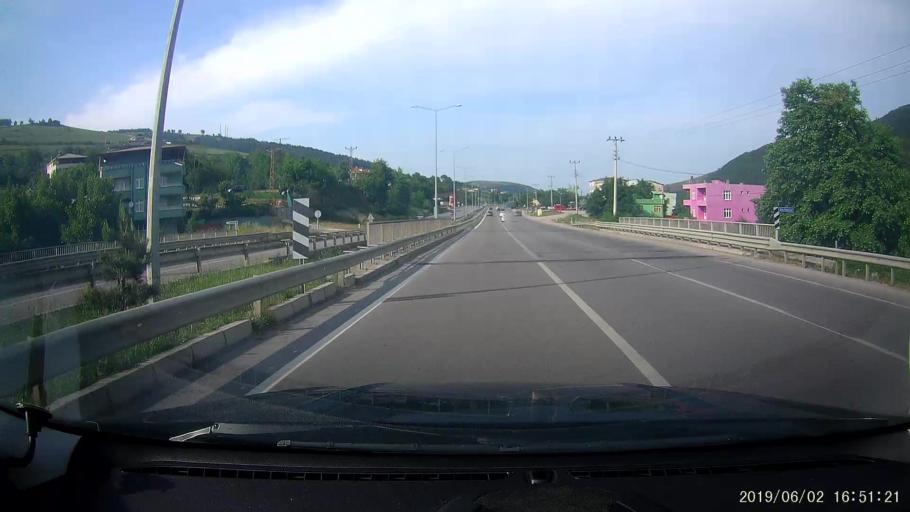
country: TR
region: Samsun
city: Taflan
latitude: 41.2726
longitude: 36.1812
